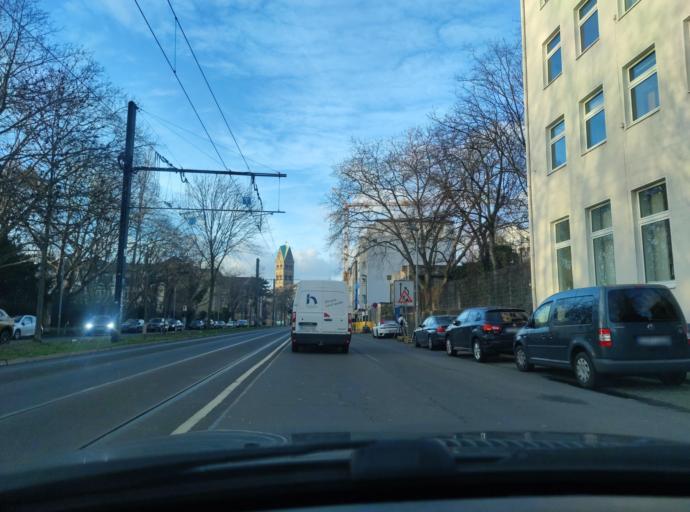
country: DE
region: North Rhine-Westphalia
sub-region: Regierungsbezirk Dusseldorf
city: Dusseldorf
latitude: 51.2295
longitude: 6.7922
